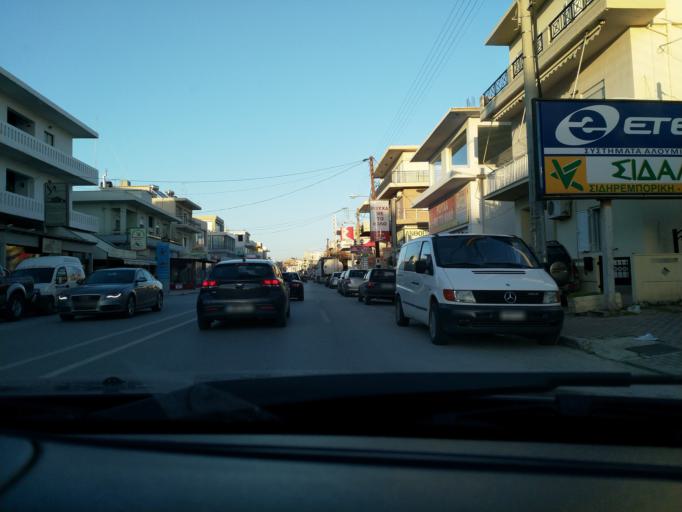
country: GR
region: Crete
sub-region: Nomos Chanias
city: Chania
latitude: 35.5079
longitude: 24.0068
